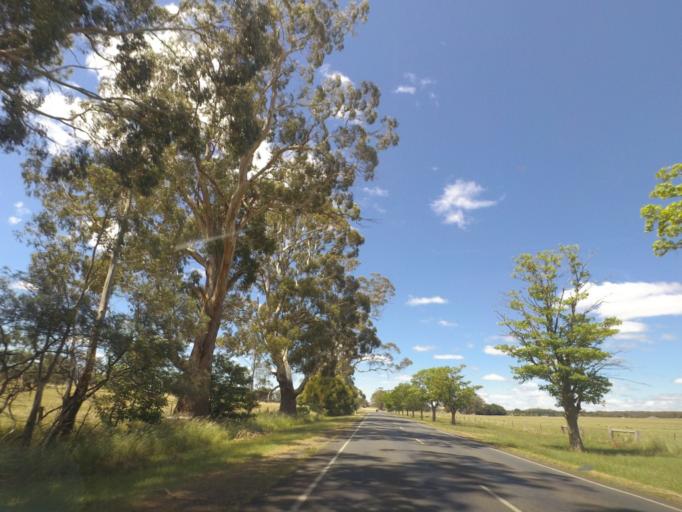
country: AU
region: Victoria
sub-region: Mount Alexander
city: Castlemaine
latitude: -37.3334
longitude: 144.1718
